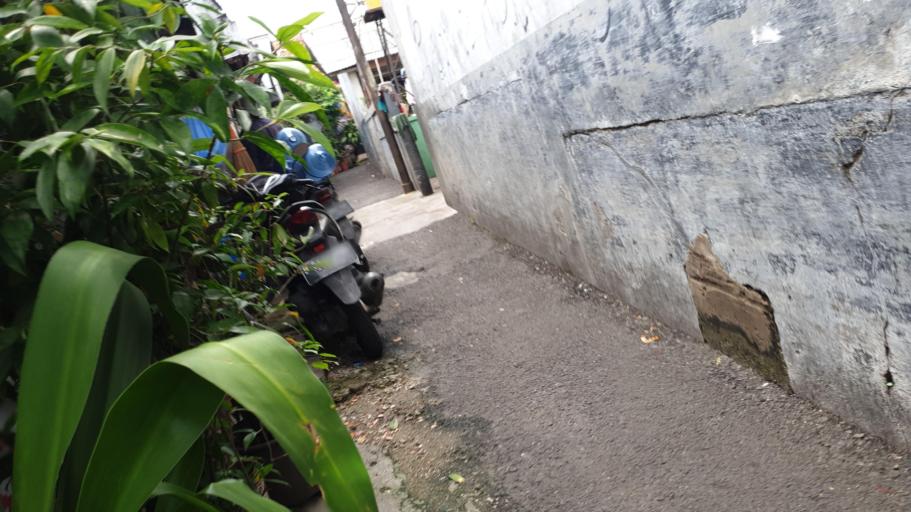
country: ID
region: Jakarta Raya
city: Jakarta
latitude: -6.2616
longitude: 106.7942
